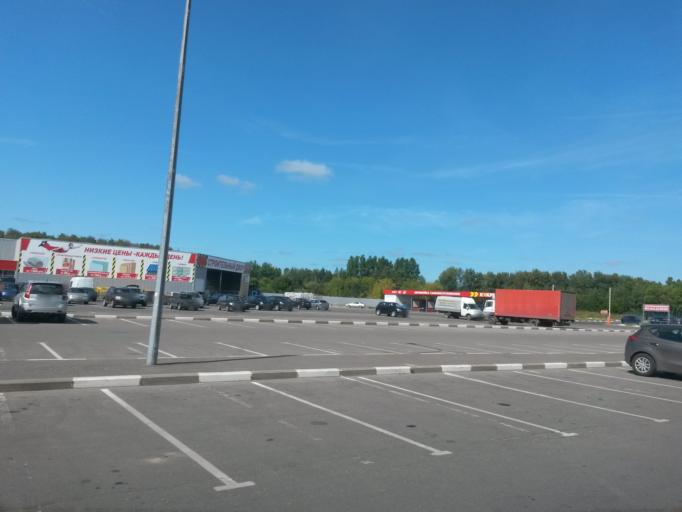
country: RU
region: Jaroslavl
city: Yaroslavl
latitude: 57.5910
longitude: 39.8957
